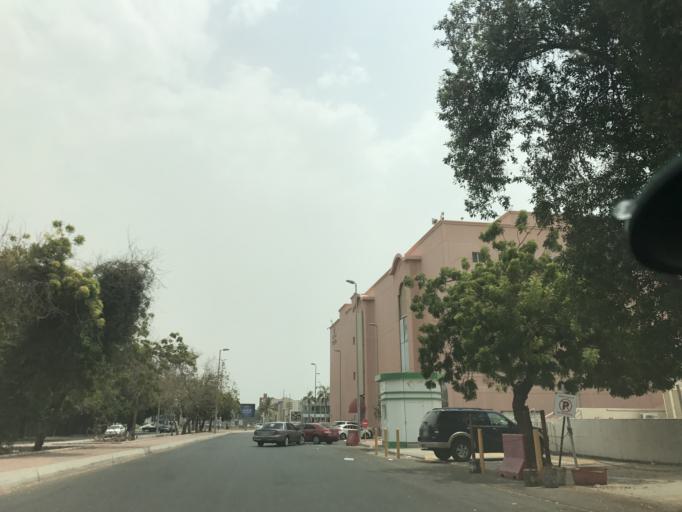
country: SA
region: Makkah
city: Jeddah
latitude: 21.5507
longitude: 39.1487
